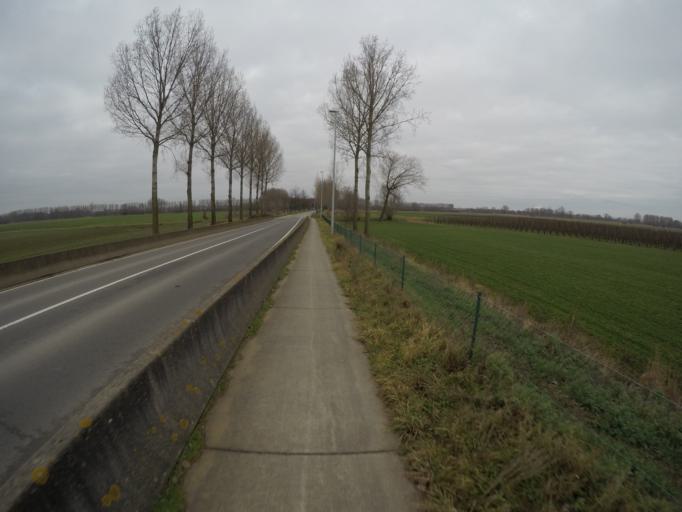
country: BE
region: Flanders
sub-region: Provincie Oost-Vlaanderen
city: Sint-Gillis-Waas
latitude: 51.2361
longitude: 4.1468
